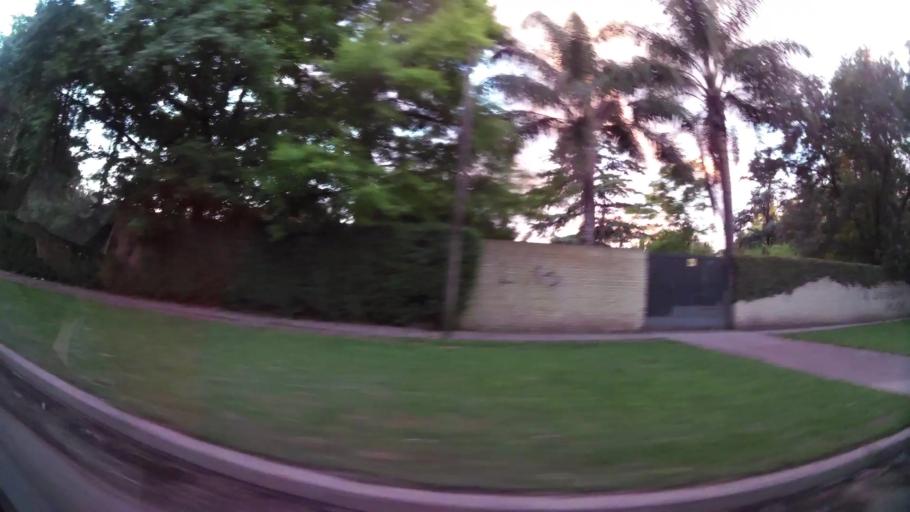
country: AR
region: Buenos Aires
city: Santa Catalina - Dique Lujan
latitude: -34.4768
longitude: -58.7700
